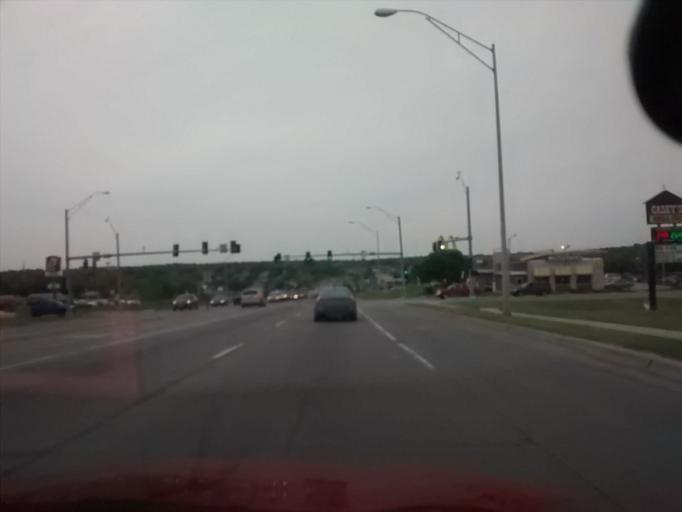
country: US
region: Nebraska
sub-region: Sarpy County
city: Offutt Air Force Base
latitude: 41.1592
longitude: -95.9434
